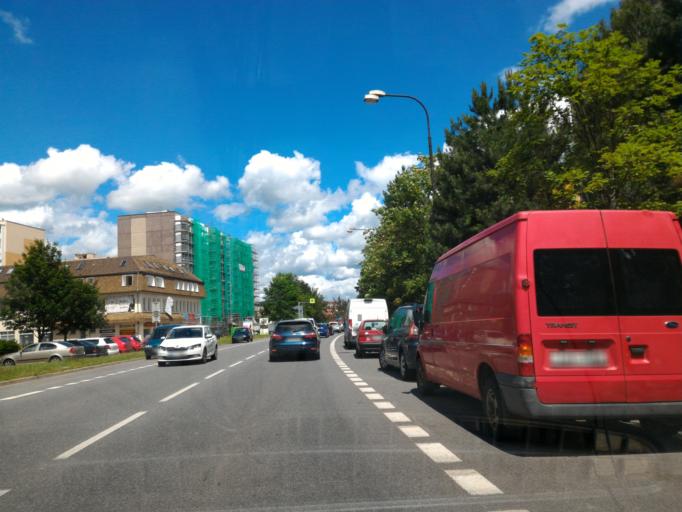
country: CZ
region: Vysocina
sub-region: Okres Zd'ar nad Sazavou
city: Zd'ar nad Sazavou
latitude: 49.5673
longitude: 15.9397
